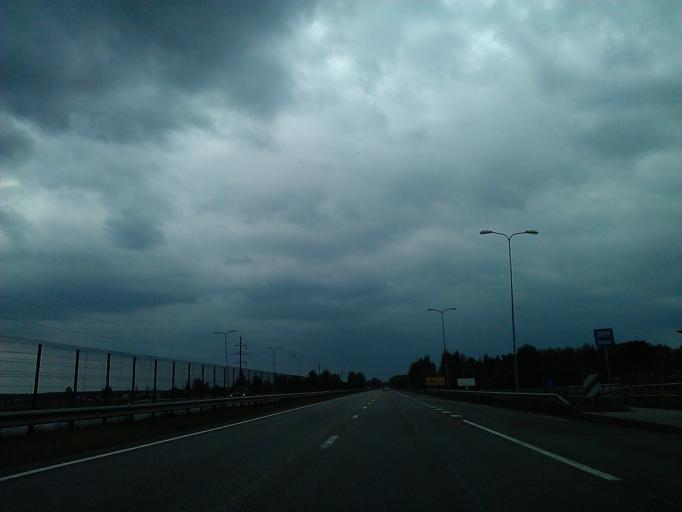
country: LV
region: Marupe
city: Marupe
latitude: 56.8274
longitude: 24.0292
